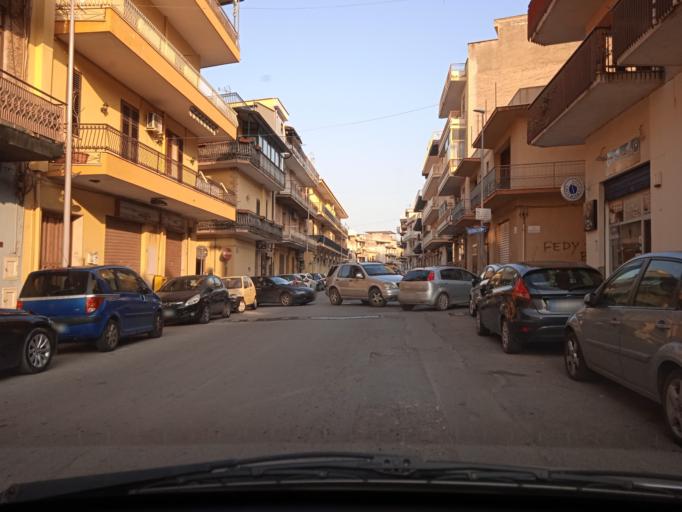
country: IT
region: Sicily
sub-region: Palermo
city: Villabate
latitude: 38.0754
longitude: 13.4475
